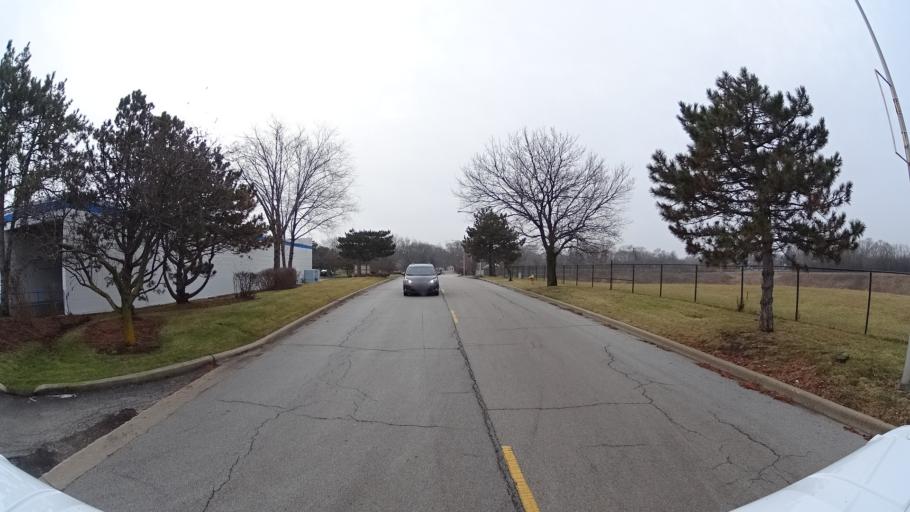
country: US
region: Illinois
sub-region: Cook County
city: Hazel Crest
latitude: 41.5733
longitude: -87.6776
